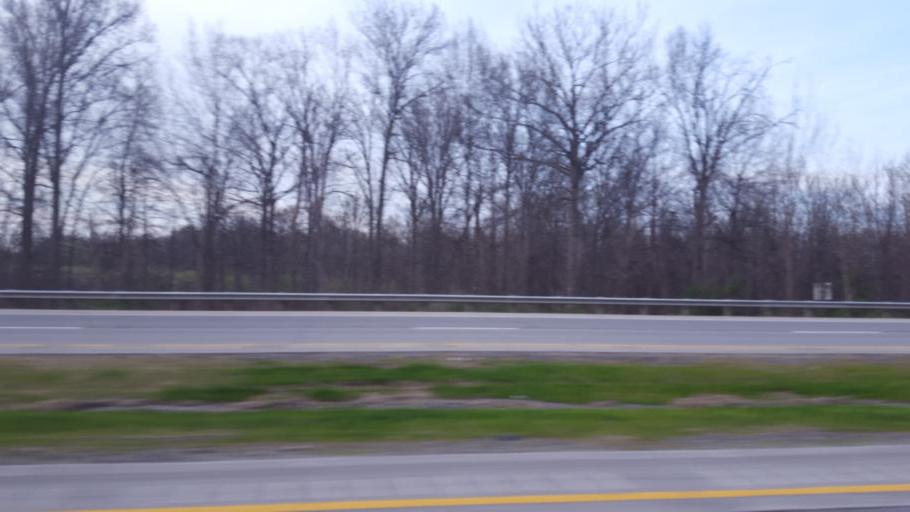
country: US
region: Ohio
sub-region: Lorain County
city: Lorain
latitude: 41.4095
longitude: -82.1561
